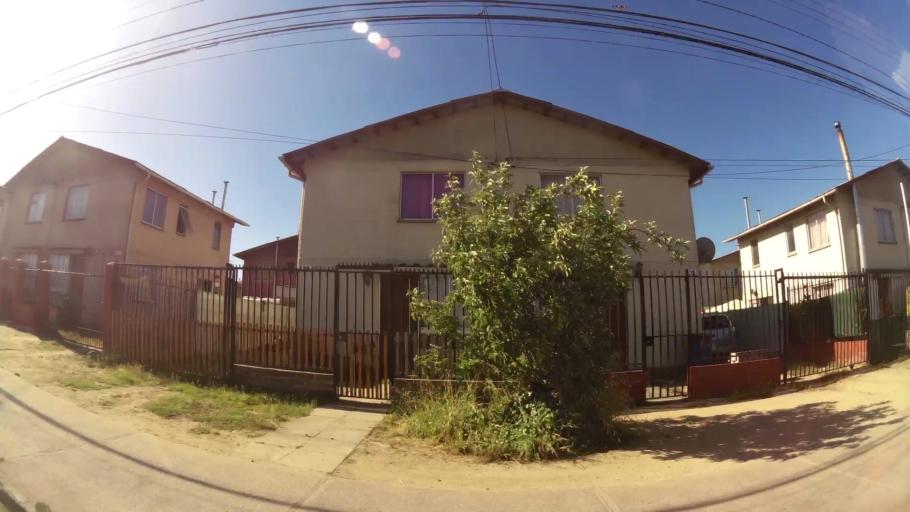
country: CL
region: Valparaiso
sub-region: Provincia de Valparaiso
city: Valparaiso
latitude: -33.1200
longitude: -71.5808
